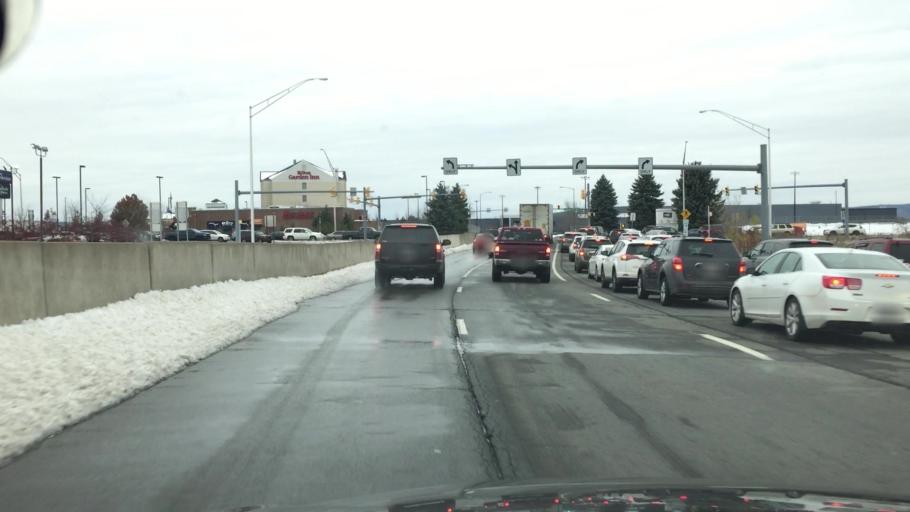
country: US
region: Pennsylvania
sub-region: Luzerne County
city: Georgetown
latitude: 41.2374
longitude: -75.8527
